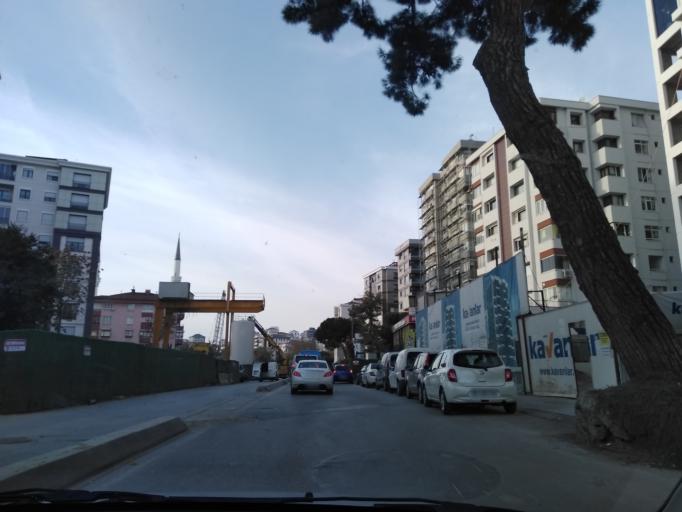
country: TR
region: Istanbul
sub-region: Atasehir
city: Atasehir
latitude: 40.9597
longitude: 29.0946
